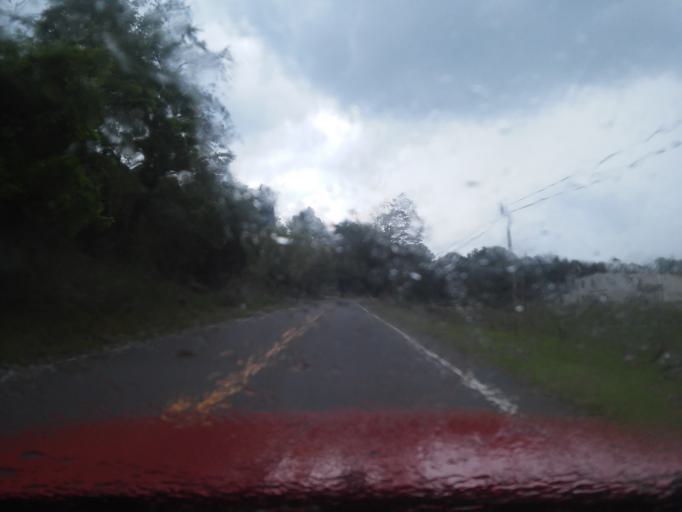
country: US
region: Virginia
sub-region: Montgomery County
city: Prices Fork
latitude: 37.3047
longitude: -80.4842
